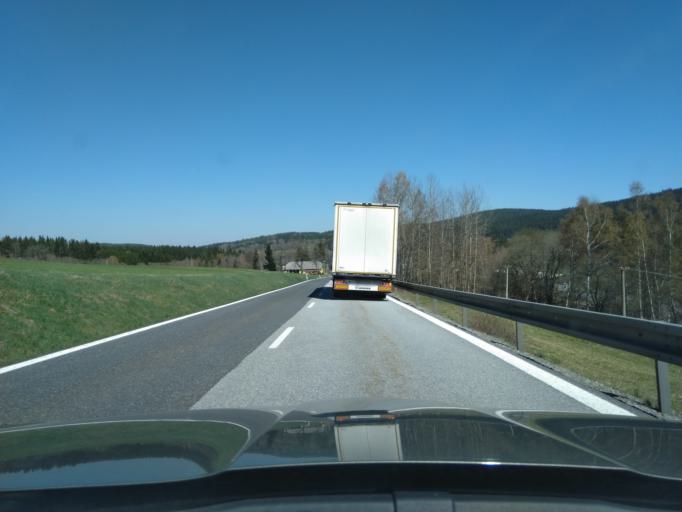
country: CZ
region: Jihocesky
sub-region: Okres Prachatice
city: Vimperk
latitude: 49.0118
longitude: 13.7682
